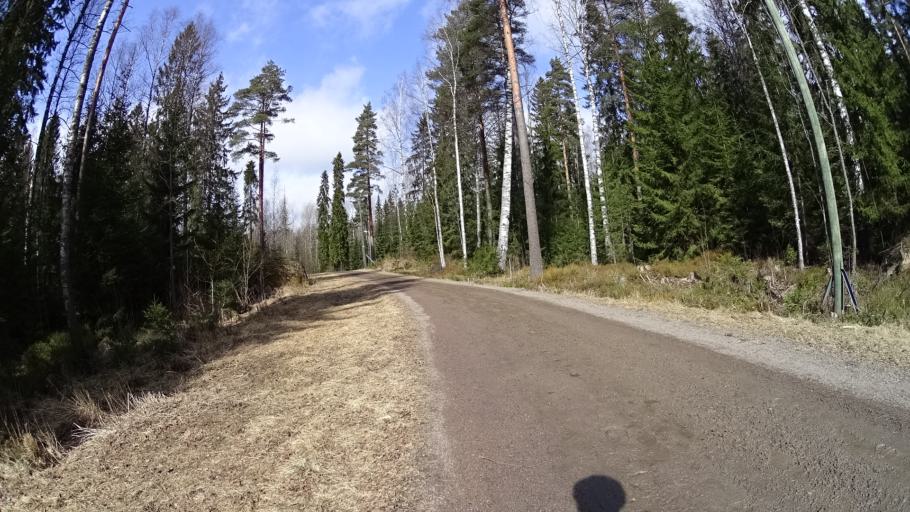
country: FI
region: Uusimaa
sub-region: Helsinki
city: Kilo
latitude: 60.2981
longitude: 24.8160
